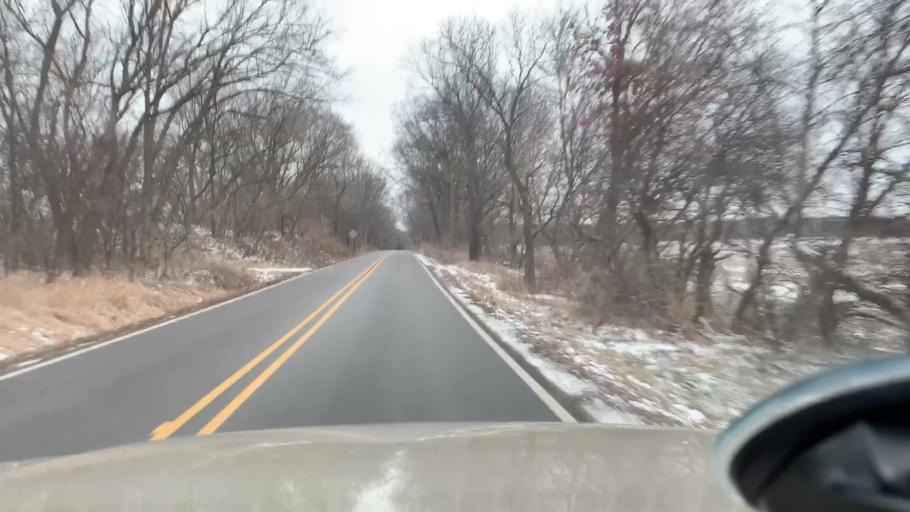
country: US
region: Michigan
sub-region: Jackson County
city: Spring Arbor
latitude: 42.2098
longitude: -84.5309
